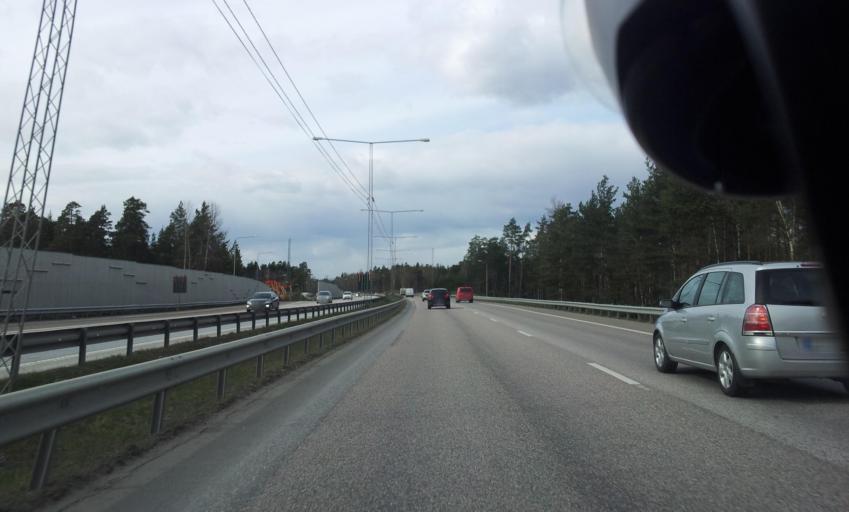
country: SE
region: Stockholm
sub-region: Jarfalla Kommun
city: Jakobsberg
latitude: 59.4472
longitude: 17.8402
